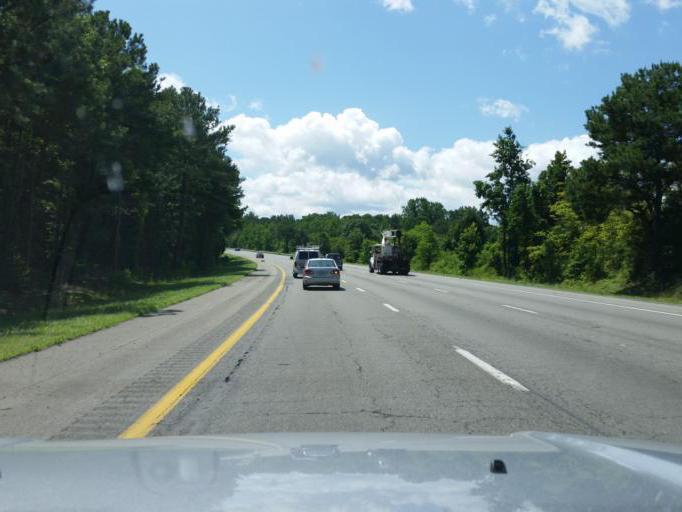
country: US
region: Virginia
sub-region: Henrico County
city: Chamberlayne
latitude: 37.6621
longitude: -77.4479
